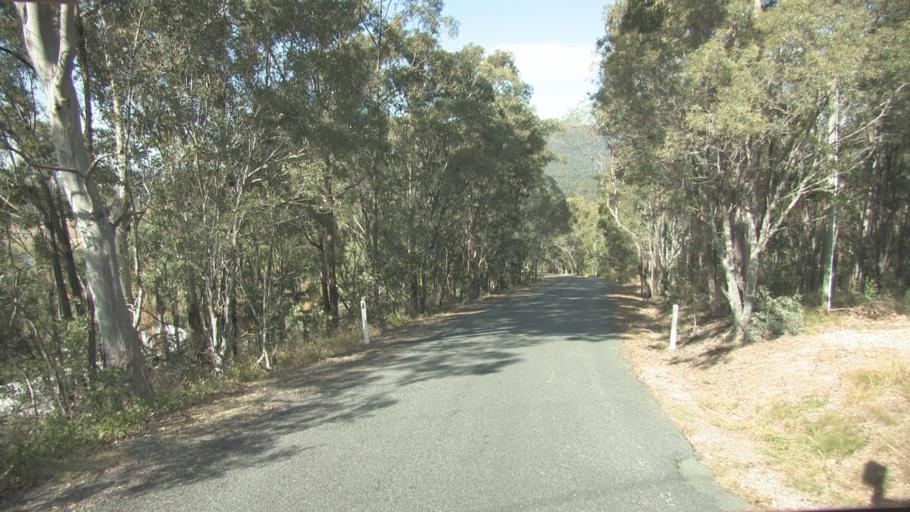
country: AU
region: Queensland
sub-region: Logan
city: Windaroo
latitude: -27.7680
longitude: 153.1862
